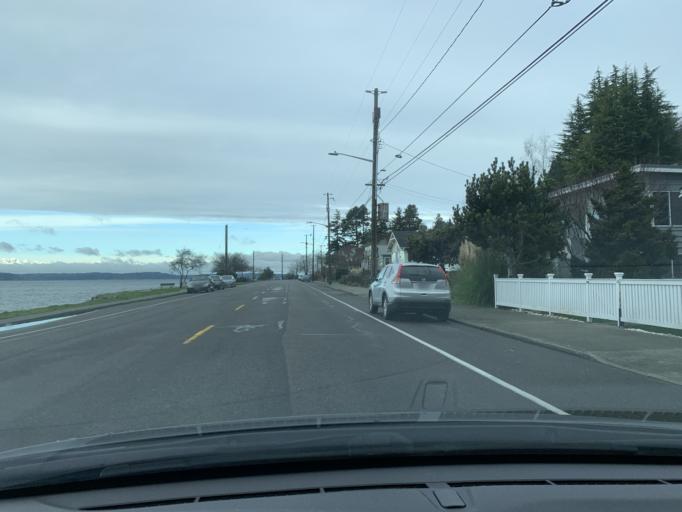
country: US
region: Washington
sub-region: King County
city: White Center
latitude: 47.5617
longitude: -122.4047
